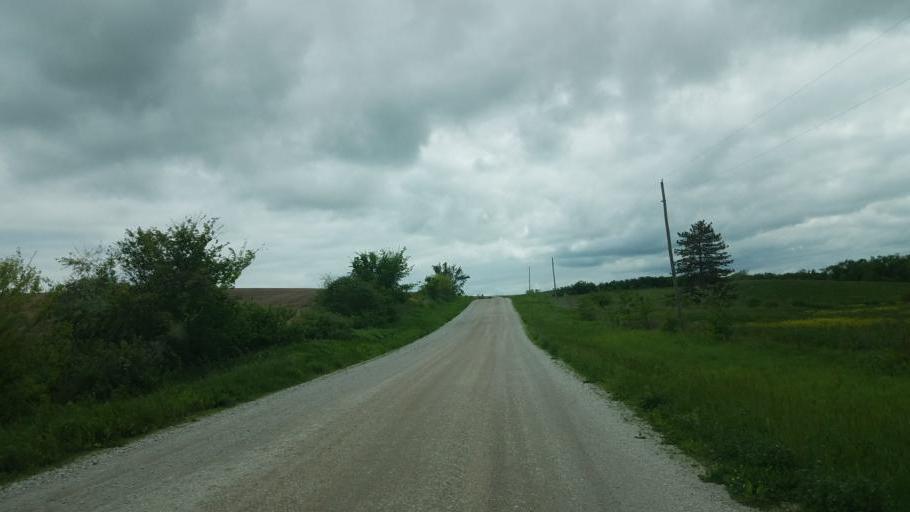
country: US
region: Iowa
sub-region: Decatur County
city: Lamoni
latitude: 40.5837
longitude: -93.8538
